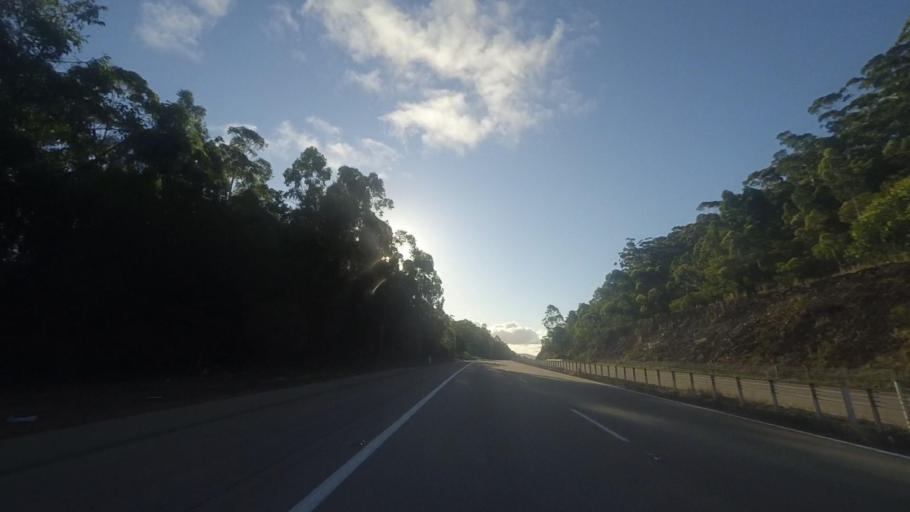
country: AU
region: New South Wales
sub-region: Great Lakes
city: Bulahdelah
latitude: -32.3880
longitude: 152.2530
